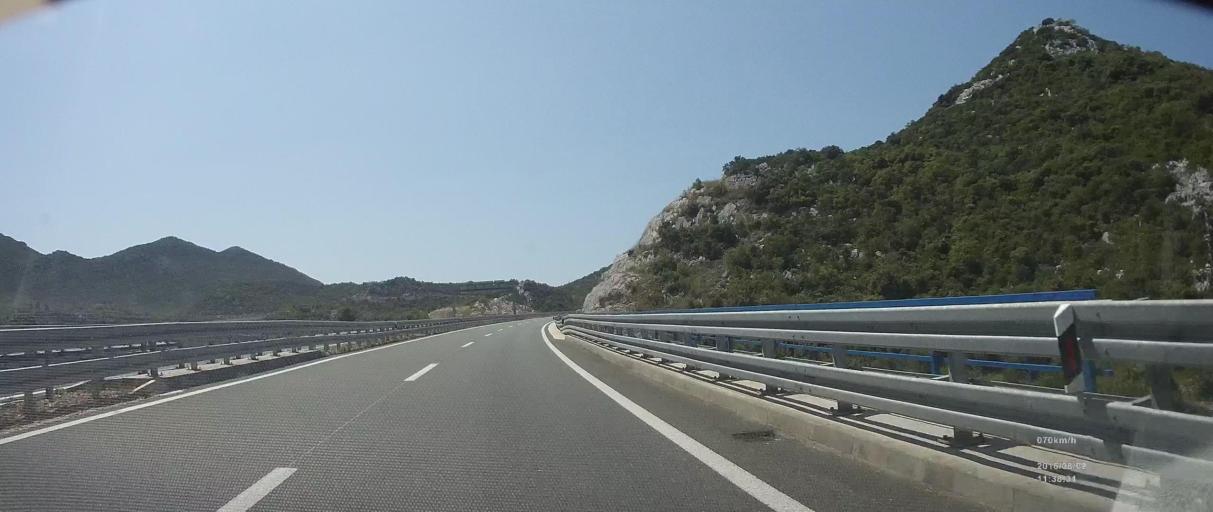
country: HR
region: Dubrovacko-Neretvanska
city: Komin
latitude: 43.0951
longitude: 17.4909
